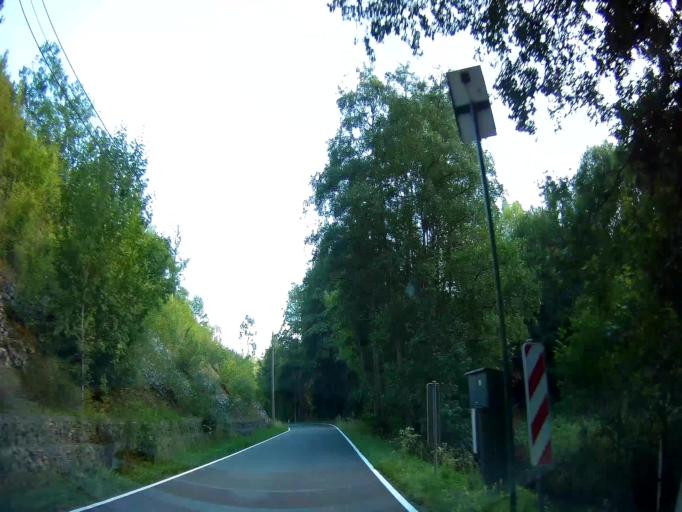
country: BE
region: Wallonia
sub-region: Province de Namur
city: Onhaye
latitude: 50.2984
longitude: 4.7769
